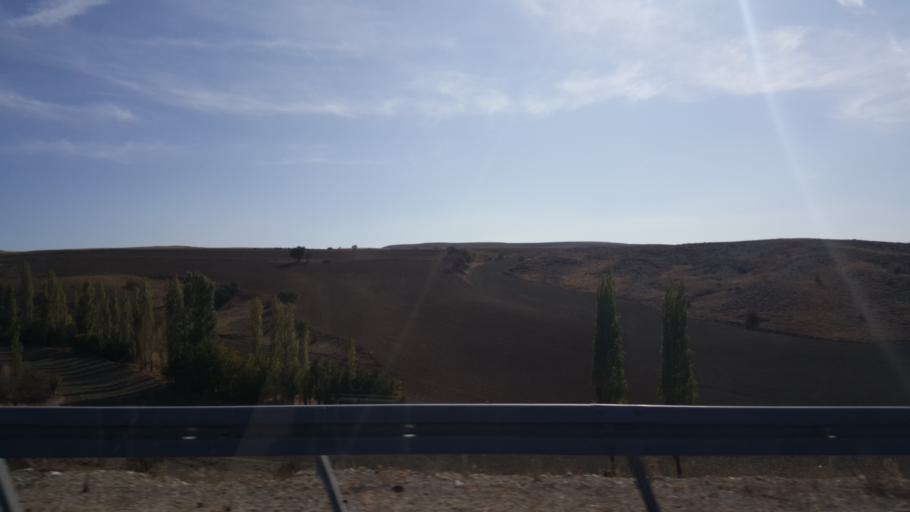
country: TR
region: Ankara
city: Haymana
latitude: 39.4021
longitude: 32.6122
